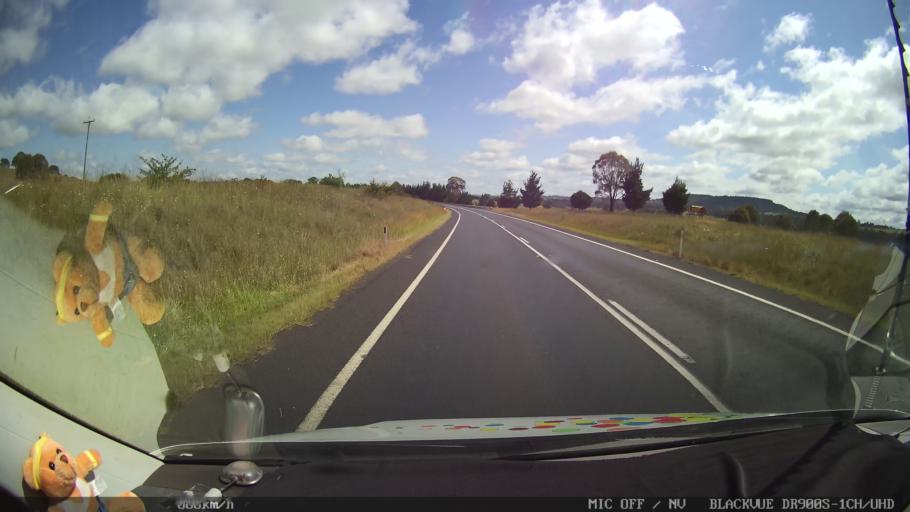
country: AU
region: New South Wales
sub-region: Glen Innes Severn
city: Glen Innes
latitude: -29.8861
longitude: 151.7338
